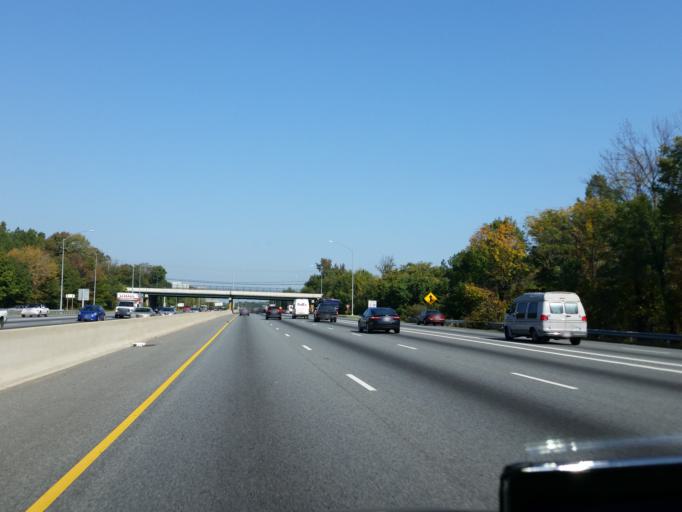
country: US
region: Maryland
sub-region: Prince George's County
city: Glenarden
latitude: 38.9148
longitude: -76.8509
